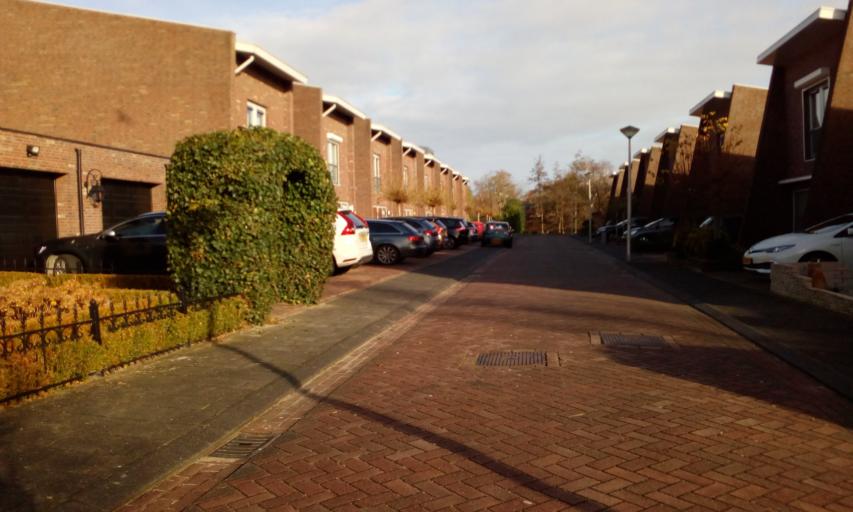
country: NL
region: South Holland
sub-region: Gemeente Lansingerland
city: Bergschenhoek
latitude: 51.9854
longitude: 4.4953
